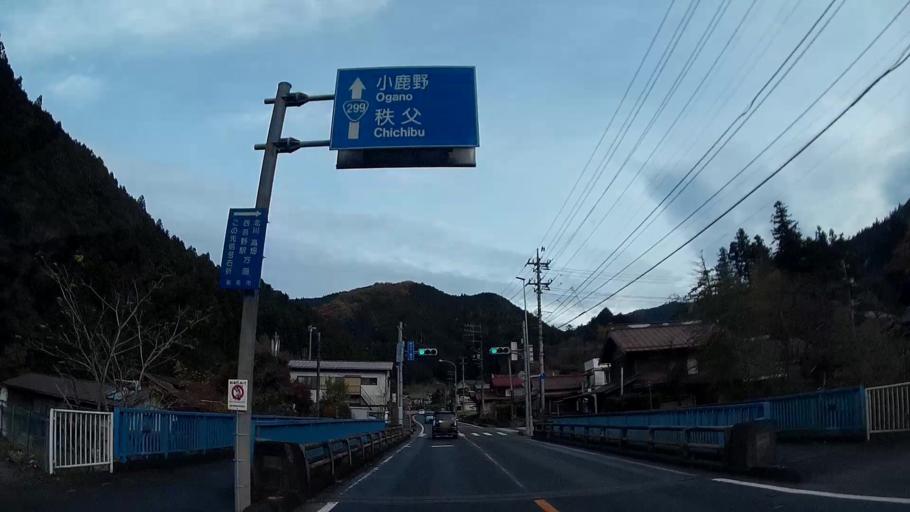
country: JP
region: Saitama
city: Morohongo
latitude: 35.9253
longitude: 139.2001
